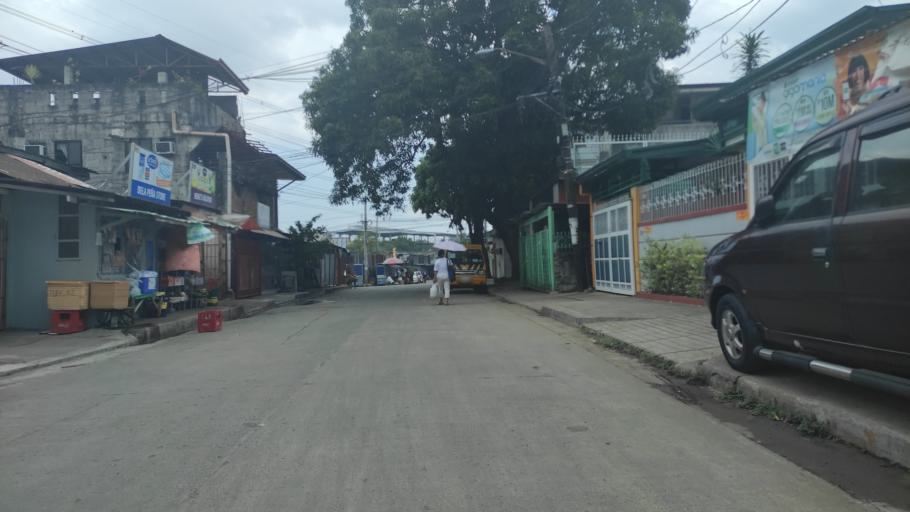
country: PH
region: Calabarzon
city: Bagong Pagasa
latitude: 14.6735
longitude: 121.0181
